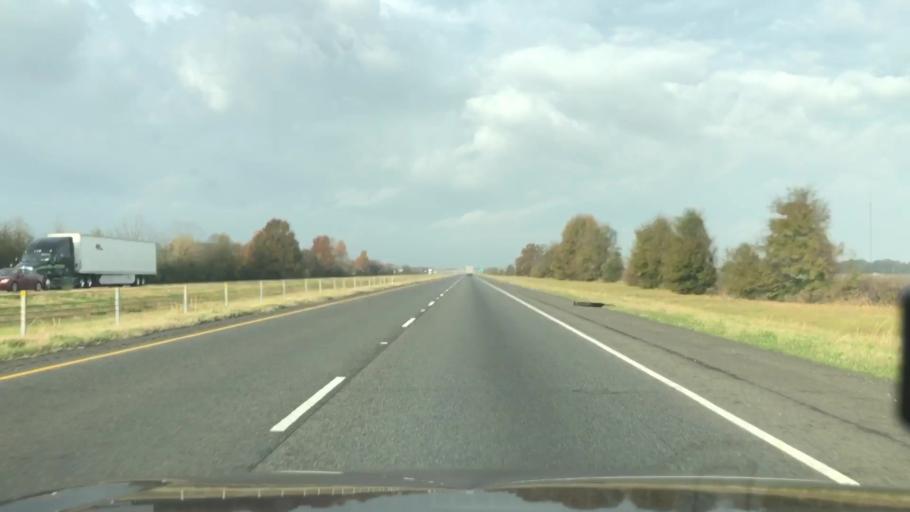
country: US
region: Louisiana
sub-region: Richland Parish
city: Delhi
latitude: 32.4283
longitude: -91.3973
